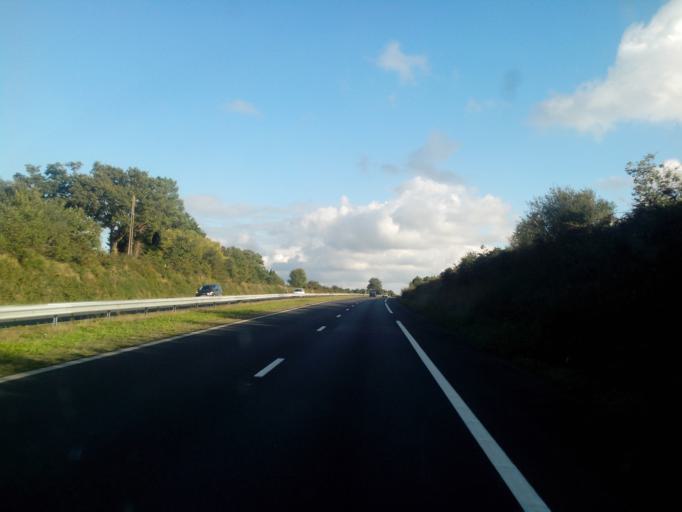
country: FR
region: Pays de la Loire
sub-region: Departement de la Loire-Atlantique
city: Pontchateau
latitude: 47.4309
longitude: -2.0640
